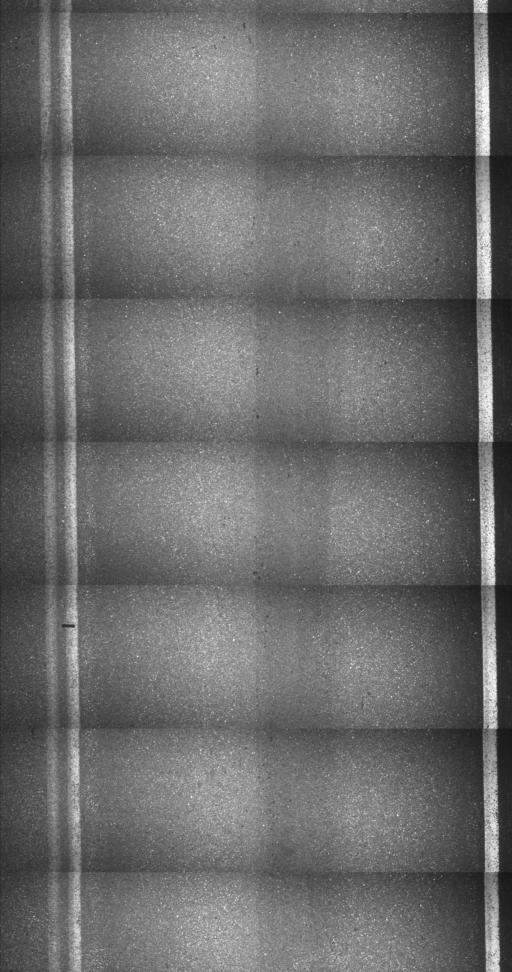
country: US
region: Vermont
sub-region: Caledonia County
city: Lyndonville
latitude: 44.7858
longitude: -71.9116
